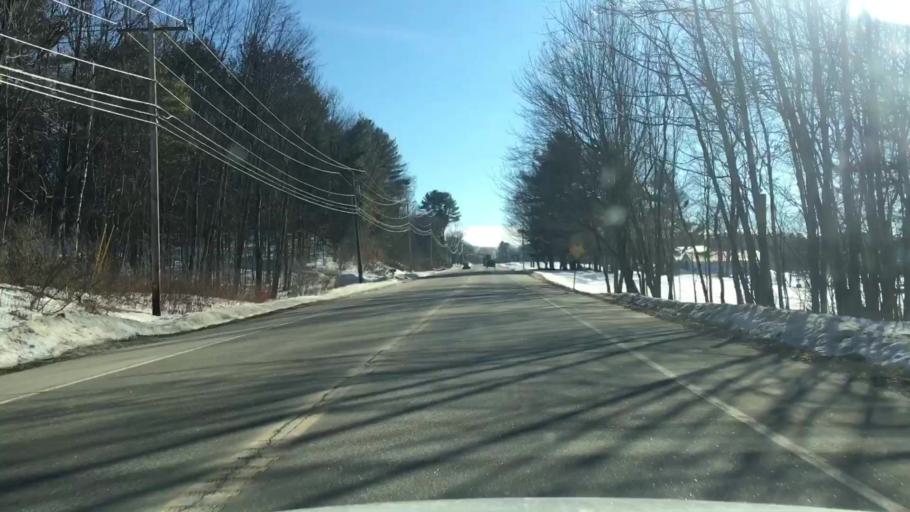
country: US
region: Maine
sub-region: Cumberland County
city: North Windham
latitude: 43.8085
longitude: -70.4035
